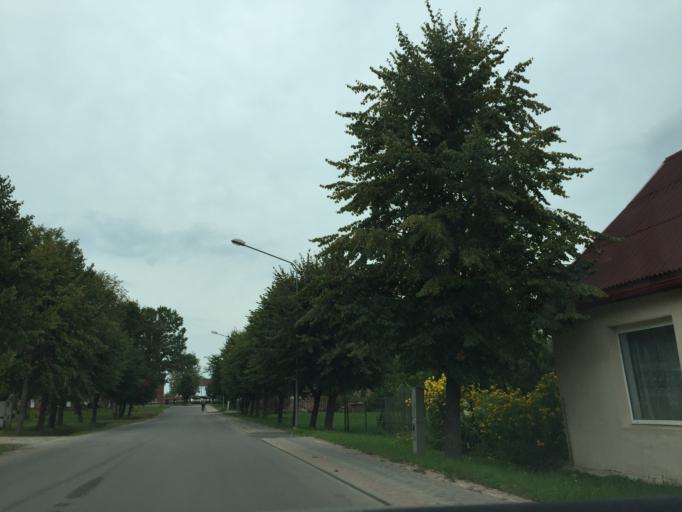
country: LV
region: Zilupes
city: Zilupe
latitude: 56.3888
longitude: 28.1242
